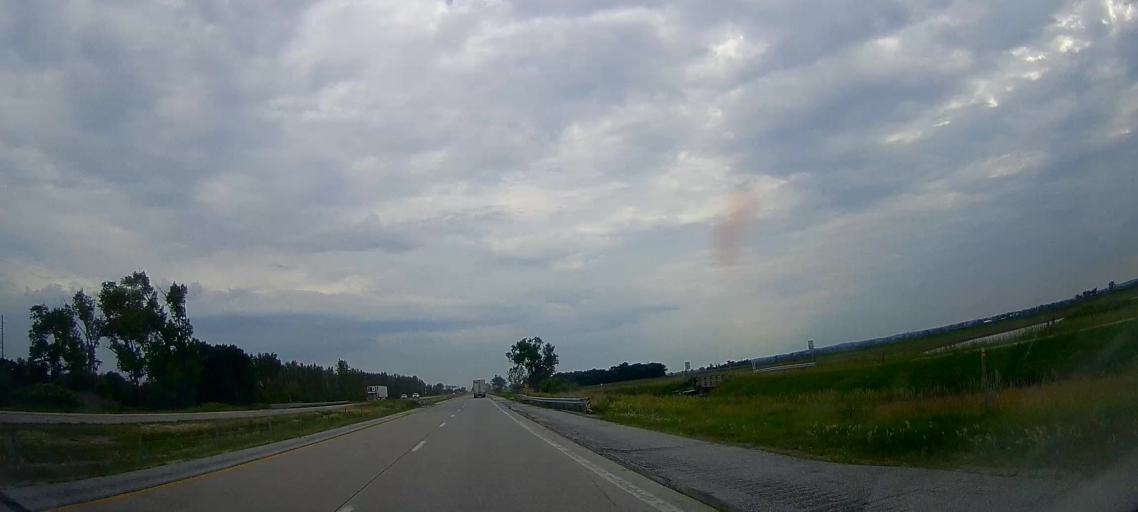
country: US
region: Iowa
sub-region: Harrison County
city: Missouri Valley
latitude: 41.4843
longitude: -95.9003
